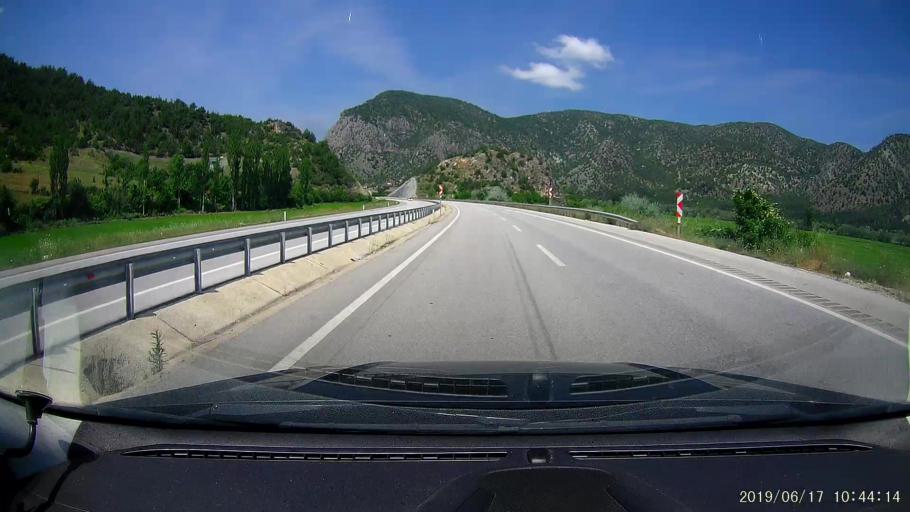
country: TR
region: Corum
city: Kargi
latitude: 41.0723
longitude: 34.5177
